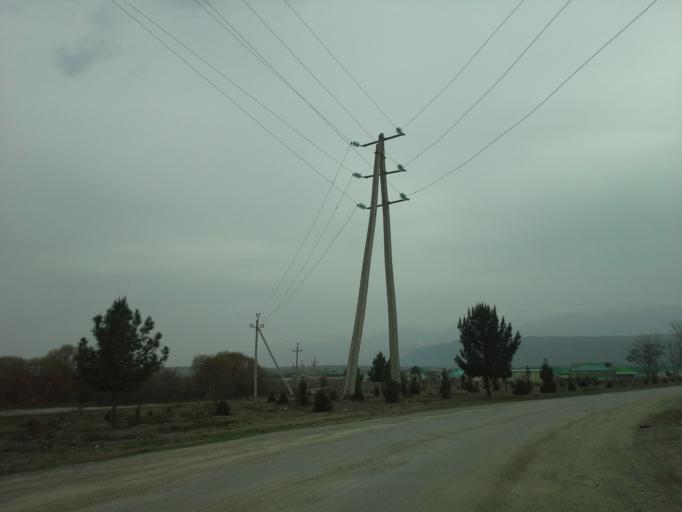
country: TM
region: Ahal
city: Abadan
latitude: 37.9827
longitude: 58.2258
